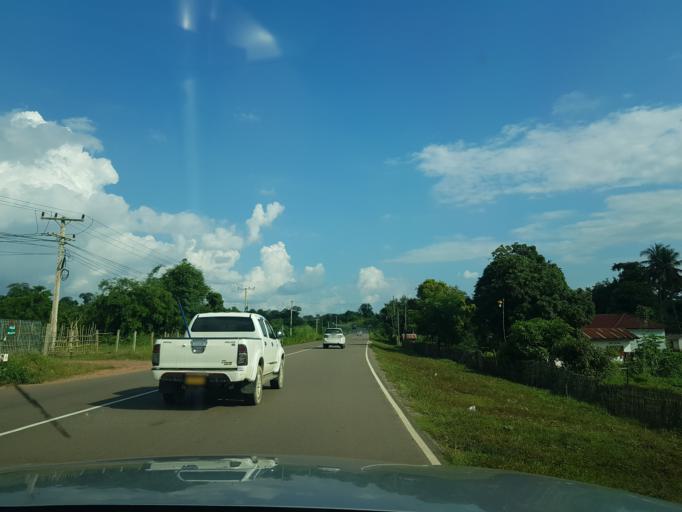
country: TH
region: Nong Khai
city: Pho Tak
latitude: 17.9937
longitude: 102.4200
